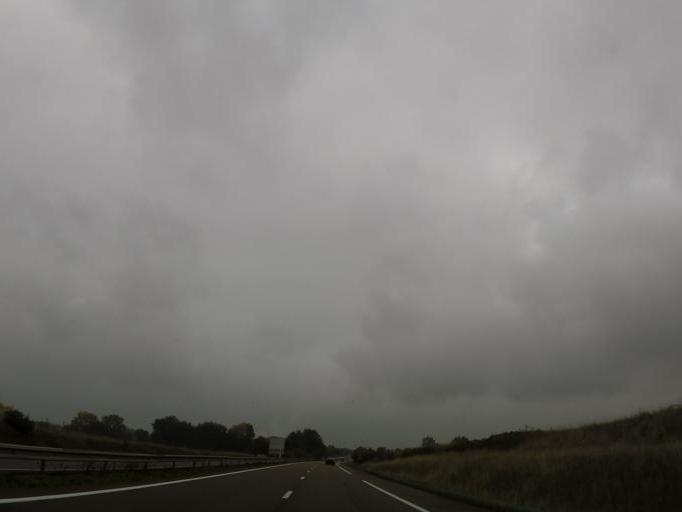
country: FR
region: Champagne-Ardenne
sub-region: Departement de la Marne
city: Sillery
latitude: 49.1988
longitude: 4.1133
